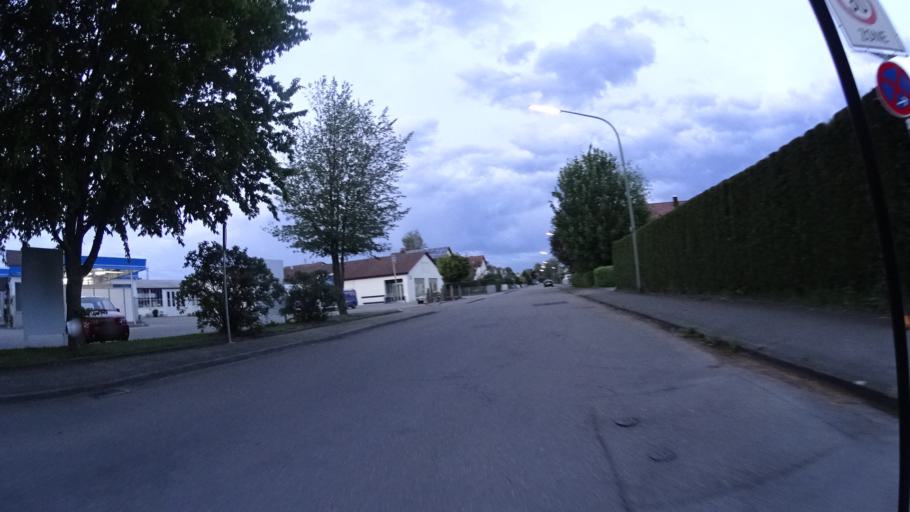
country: DE
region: Bavaria
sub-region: Swabia
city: Pfaffenhofen an der Roth
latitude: 48.3581
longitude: 10.1602
